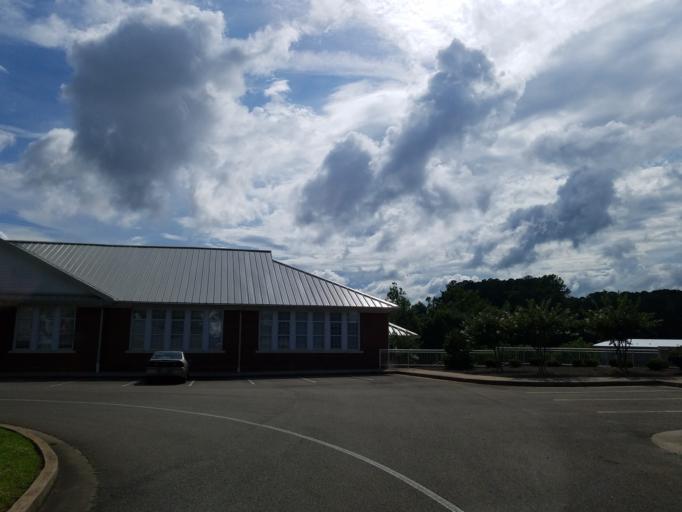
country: US
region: Georgia
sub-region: Pickens County
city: Jasper
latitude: 34.4690
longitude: -84.4332
